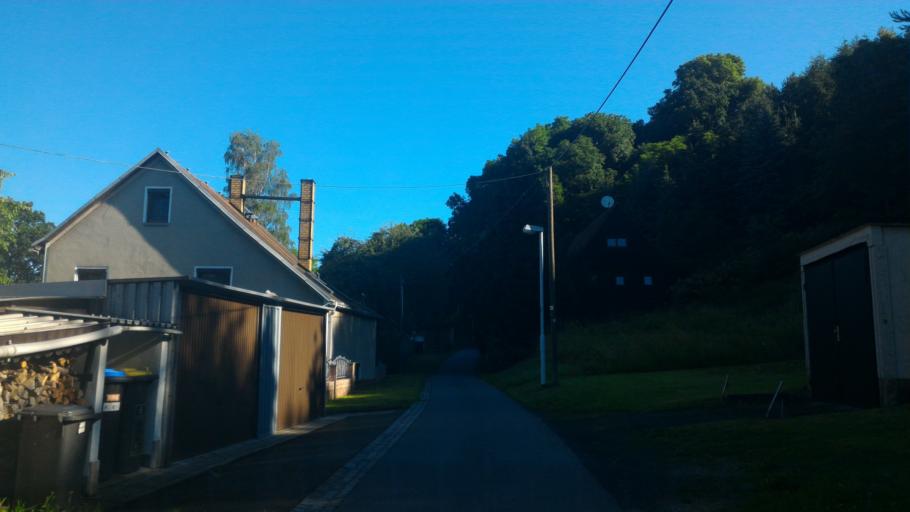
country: DE
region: Saxony
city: Mittelherwigsdorf
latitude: 50.9207
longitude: 14.7474
